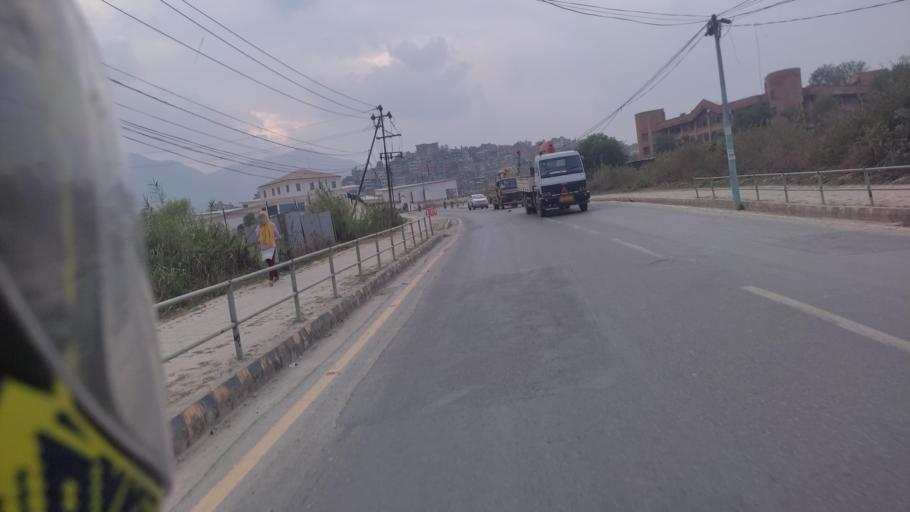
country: NP
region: Central Region
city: Kirtipur
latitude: 27.6759
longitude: 85.2867
